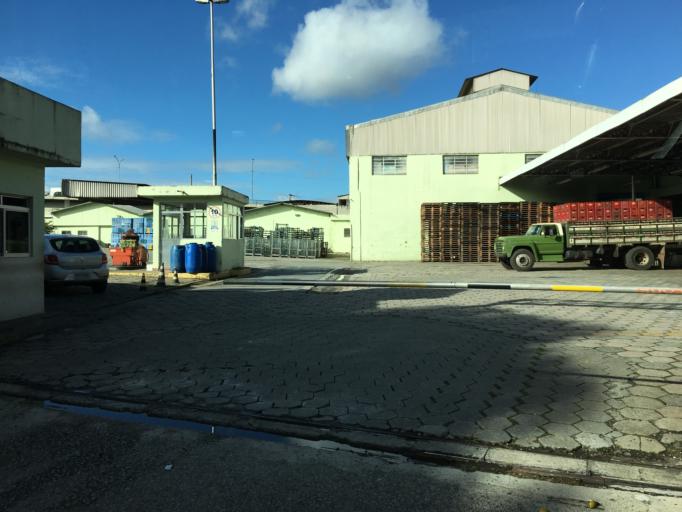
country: BR
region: Sao Paulo
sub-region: Osasco
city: Osasco
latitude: -23.5194
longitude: -46.7486
